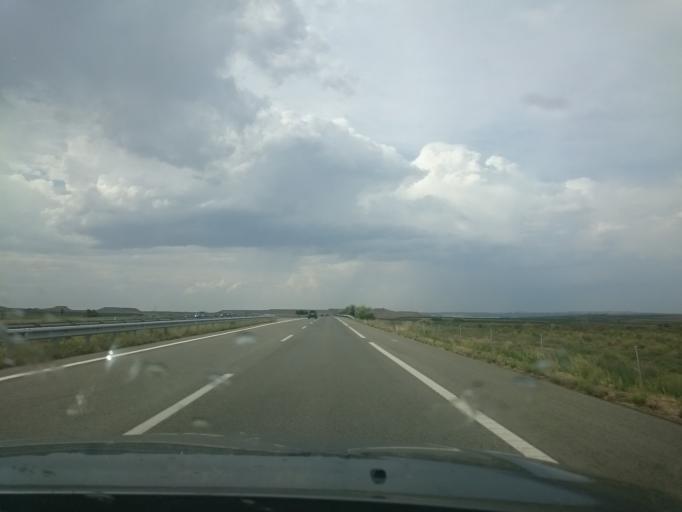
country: ES
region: La Rioja
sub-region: Provincia de La Rioja
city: Rincon de Soto
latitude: 42.1804
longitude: -1.8380
